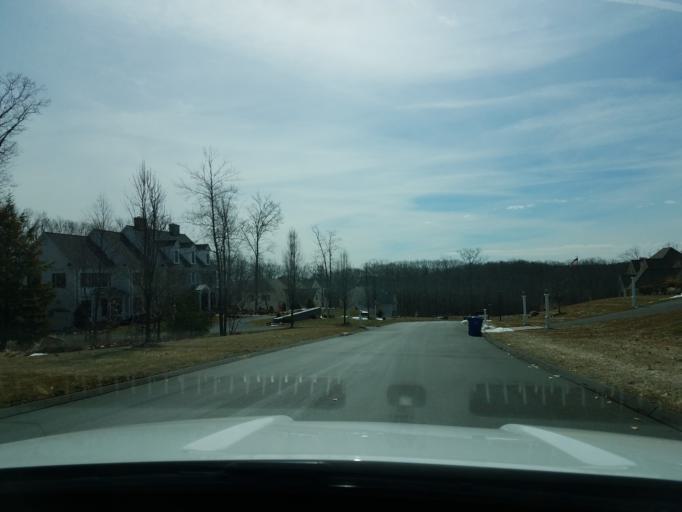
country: US
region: Connecticut
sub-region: Hartford County
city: Collinsville
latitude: 41.8043
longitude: -72.9002
